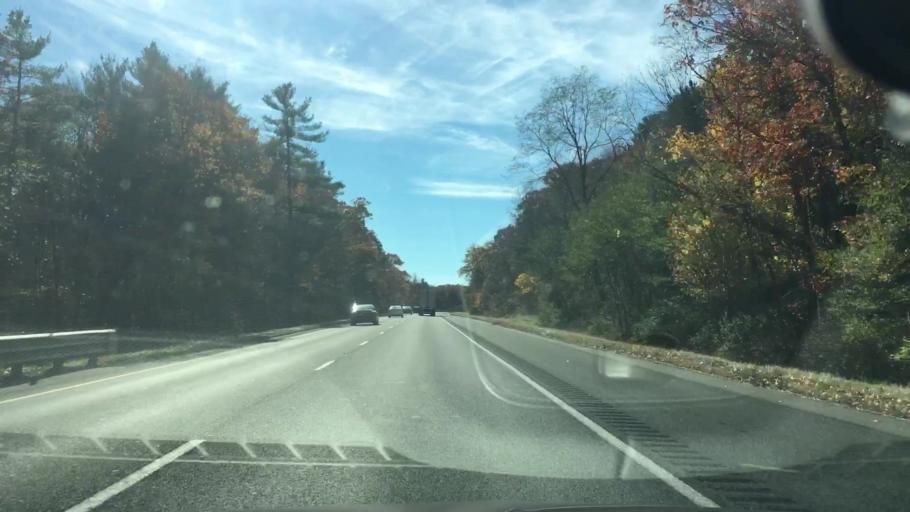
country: US
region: Massachusetts
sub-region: Hampden County
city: Holyoke
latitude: 42.2496
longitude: -72.6239
